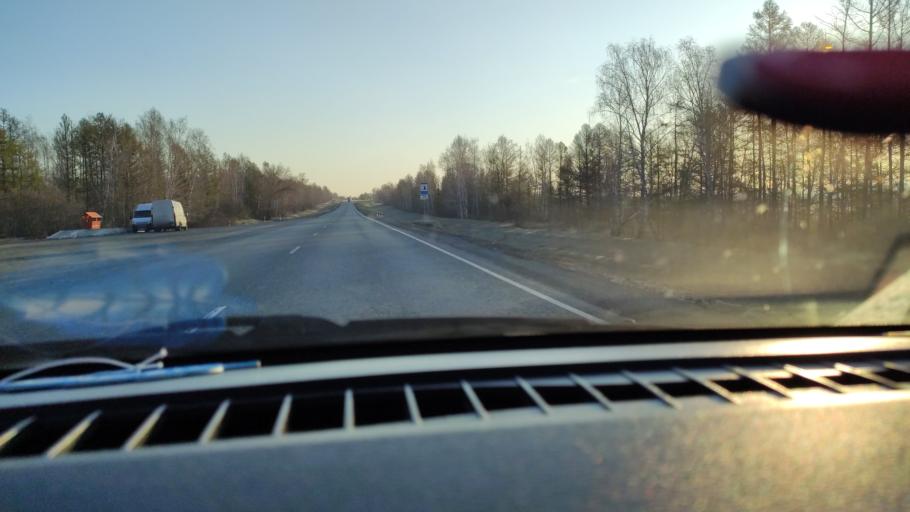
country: RU
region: Saratov
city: Sennoy
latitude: 52.1288
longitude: 46.8583
